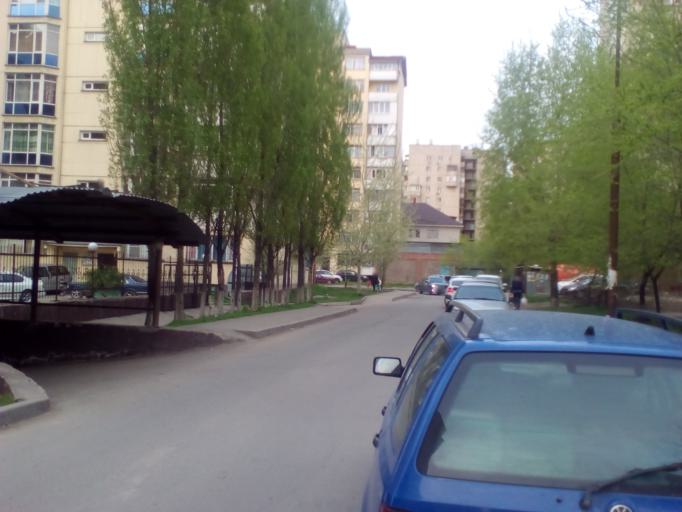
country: KZ
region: Almaty Qalasy
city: Almaty
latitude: 43.2395
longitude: 76.8252
